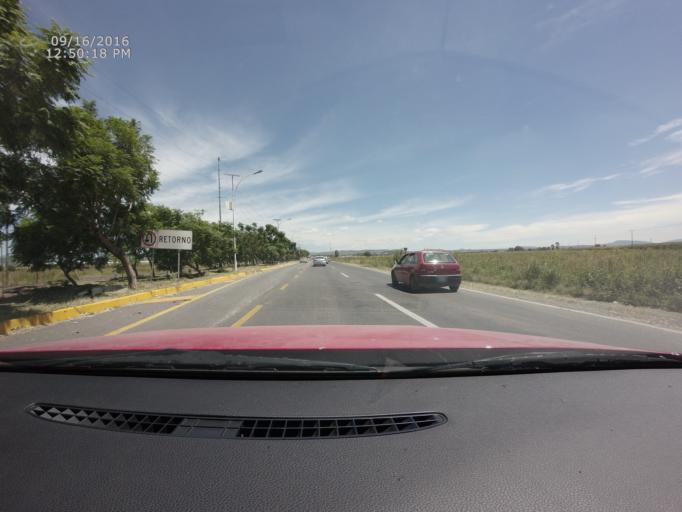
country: MX
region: Queretaro
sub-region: Colon
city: Purisima de Cubos (La Purisima)
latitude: 20.6074
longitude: -100.1641
